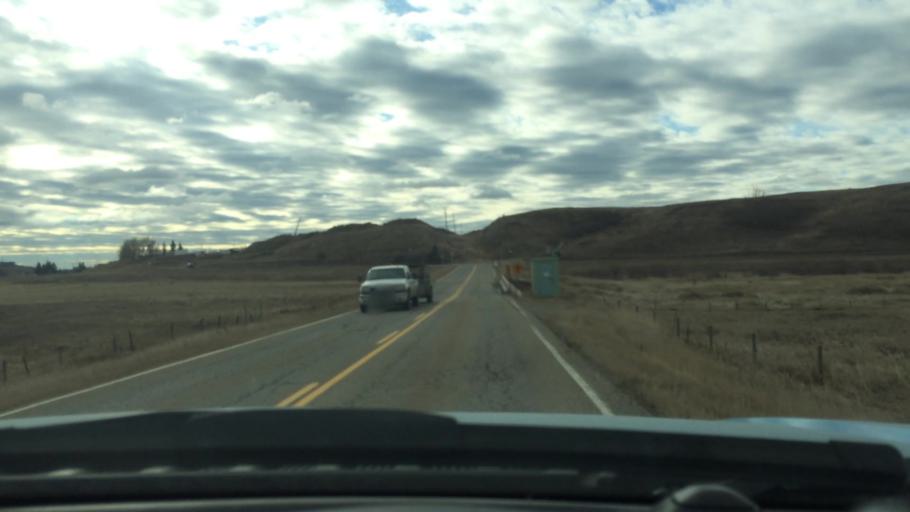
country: CA
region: Alberta
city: Calgary
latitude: 51.1906
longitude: -114.1412
